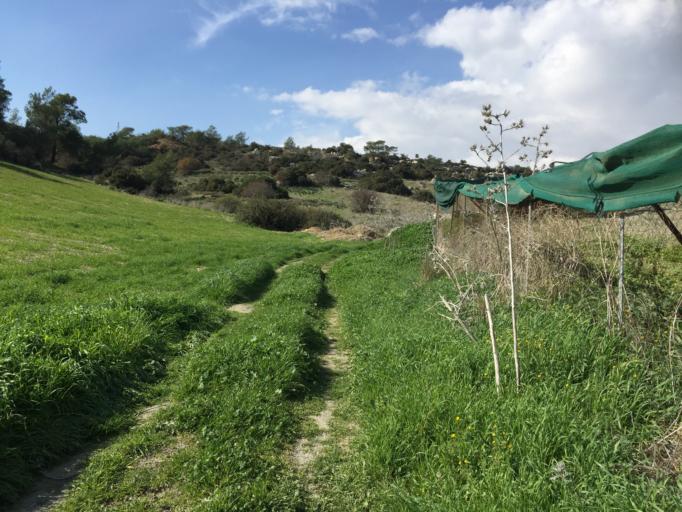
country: CY
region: Larnaka
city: Agios Tychon
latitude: 34.7426
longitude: 33.1396
